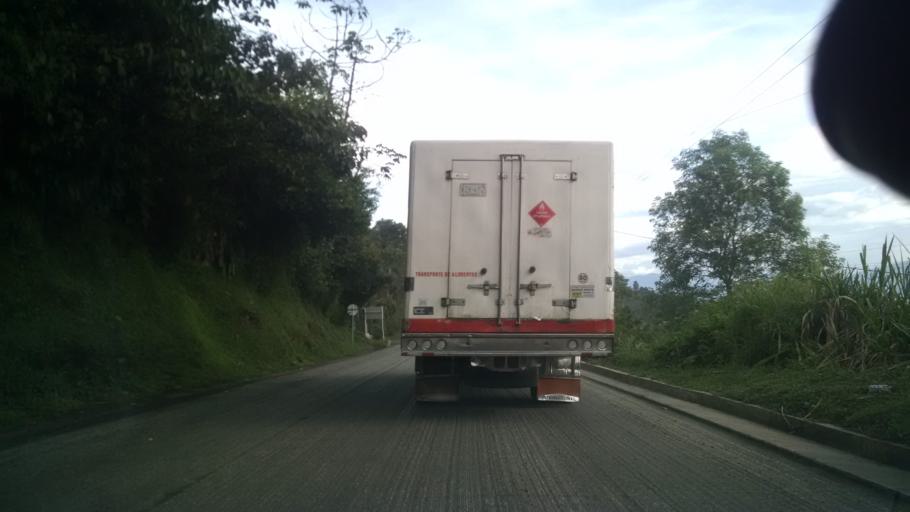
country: CO
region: Antioquia
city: Santa Barbara
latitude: 5.9140
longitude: -75.5769
